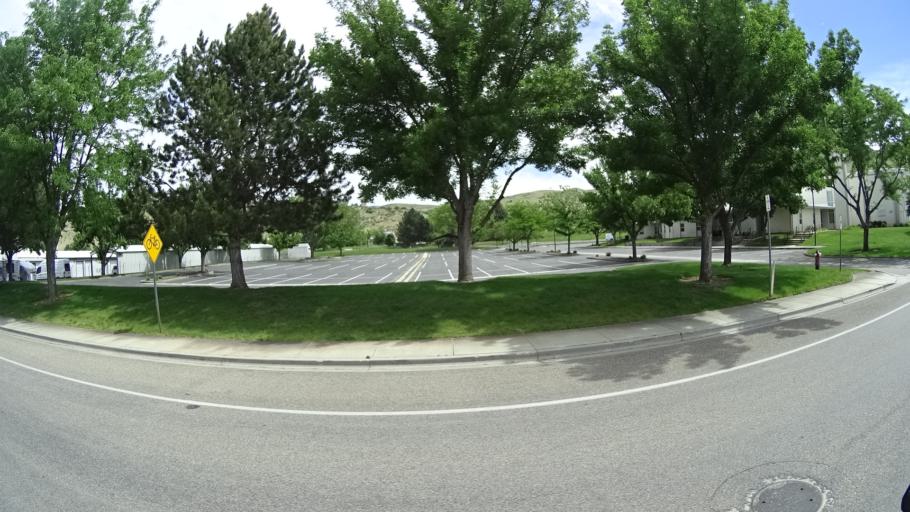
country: US
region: Idaho
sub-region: Ada County
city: Boise
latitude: 43.5987
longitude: -116.1656
